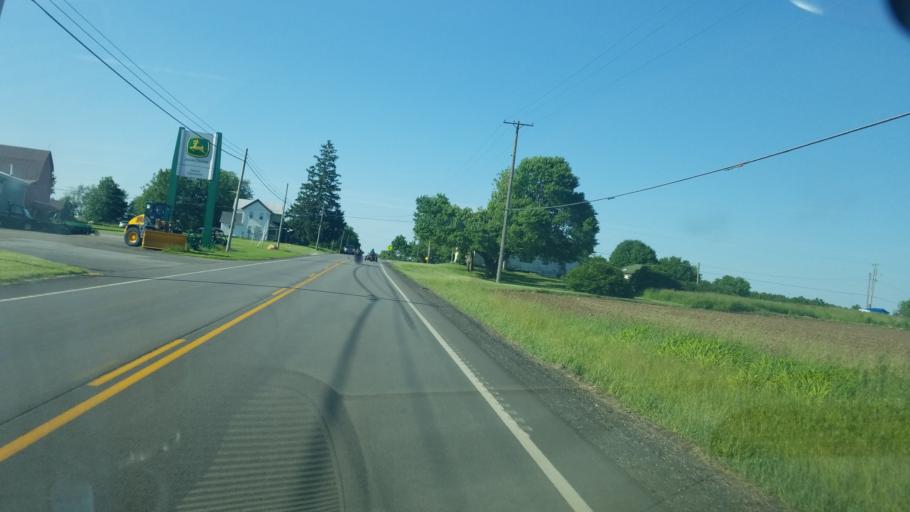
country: US
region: Ohio
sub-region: Wayne County
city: Smithville
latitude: 40.8933
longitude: -81.9165
